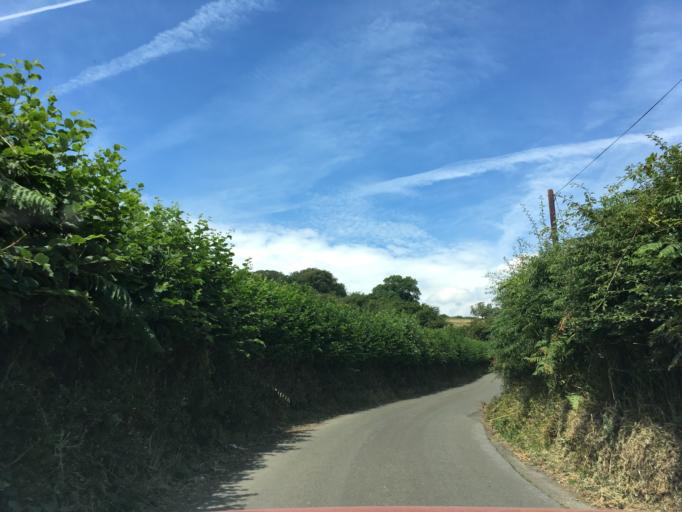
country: GB
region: Wales
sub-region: Caerphilly County Borough
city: Risca
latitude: 51.5922
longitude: -3.1064
